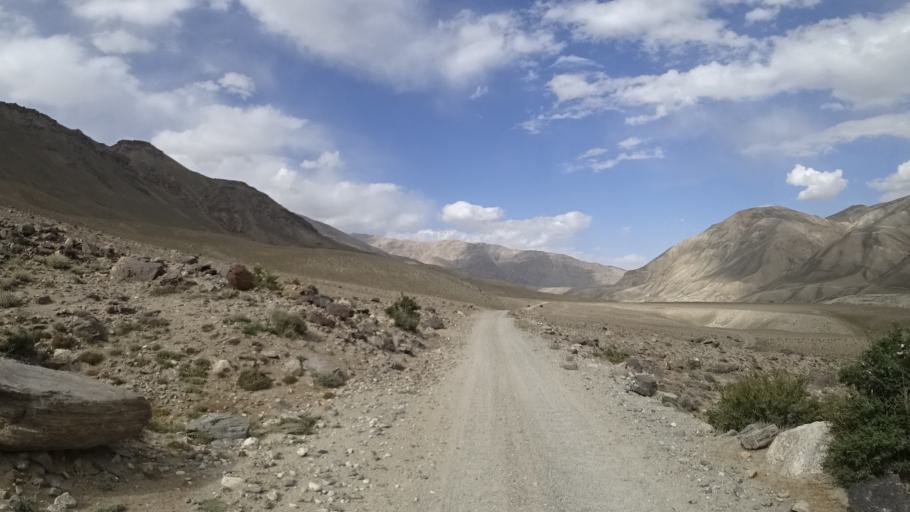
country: AF
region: Badakhshan
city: Khandud
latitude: 37.1906
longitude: 72.7616
